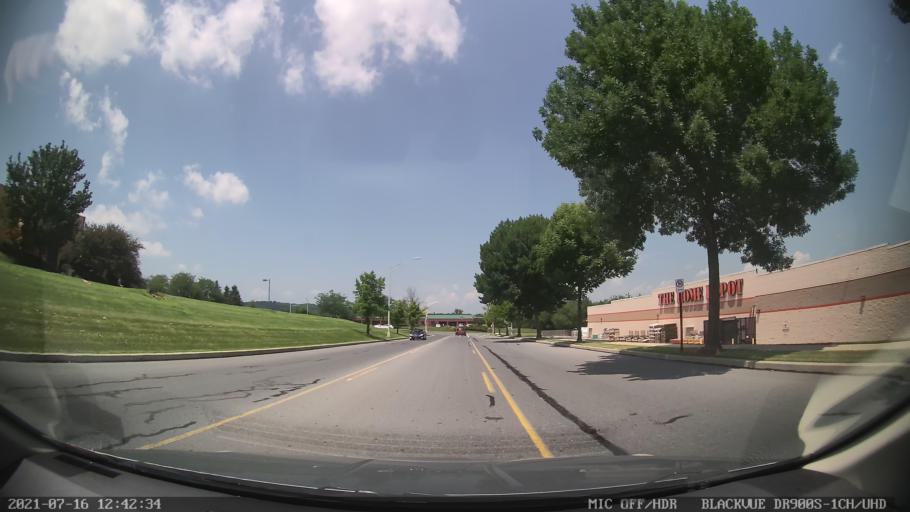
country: US
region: Pennsylvania
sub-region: Berks County
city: Wyomissing Hills
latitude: 40.3480
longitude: -75.9680
